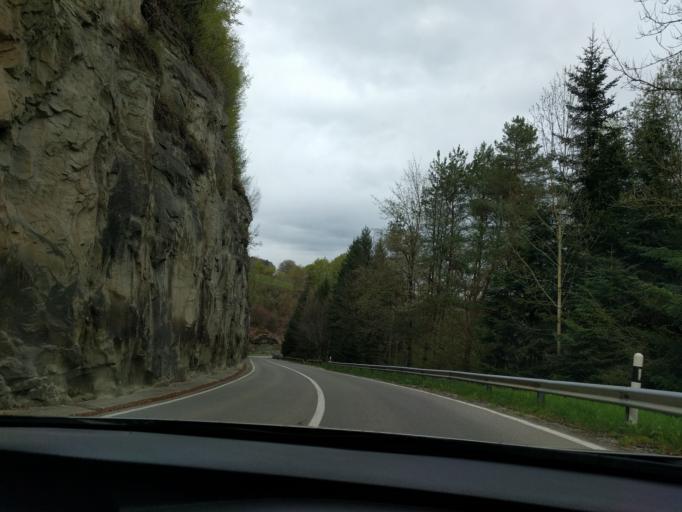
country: CH
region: Fribourg
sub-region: Sense District
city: Heitenried
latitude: 46.8223
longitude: 7.3101
